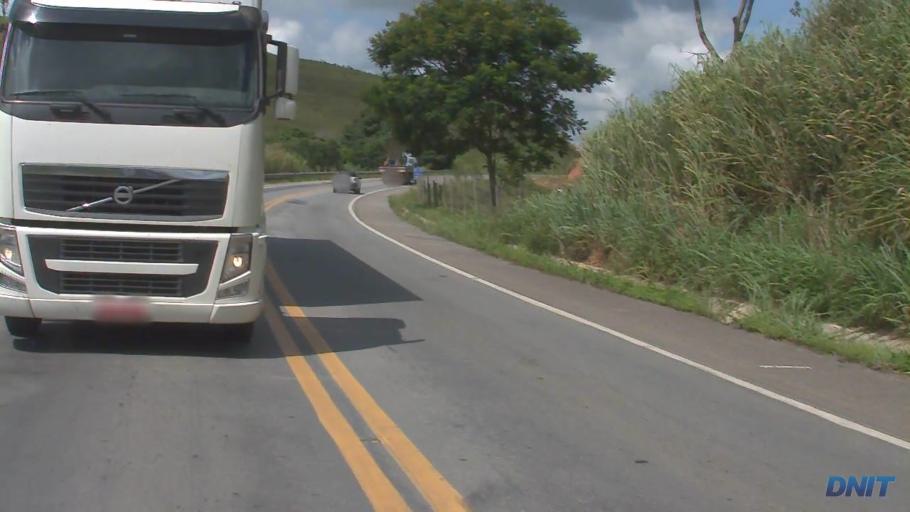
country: BR
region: Minas Gerais
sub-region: Governador Valadares
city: Governador Valadares
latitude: -19.0308
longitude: -42.1484
